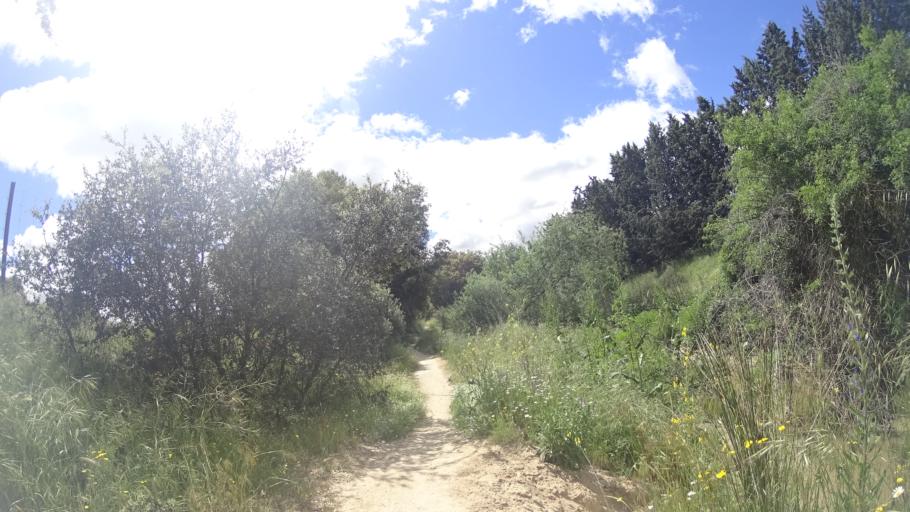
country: ES
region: Madrid
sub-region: Provincia de Madrid
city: Villaviciosa de Odon
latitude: 40.3910
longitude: -3.9436
